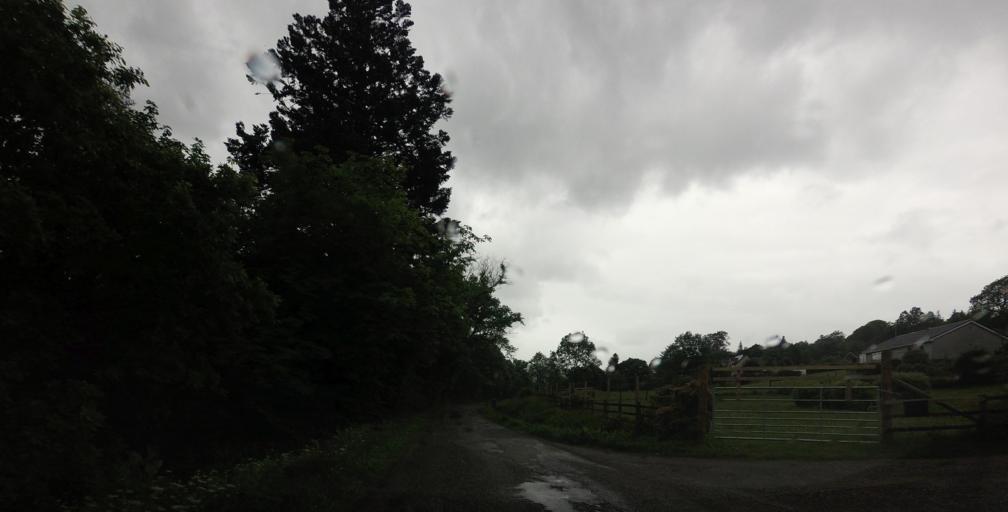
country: GB
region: Scotland
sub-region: Argyll and Bute
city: Oban
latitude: 56.6999
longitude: -5.5709
